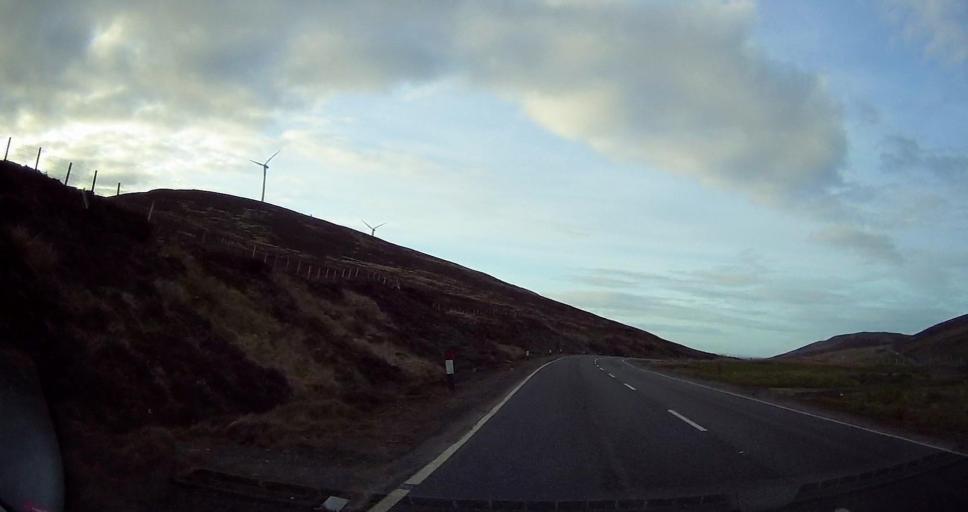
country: GB
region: Scotland
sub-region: Shetland Islands
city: Lerwick
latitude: 60.1562
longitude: -1.2345
